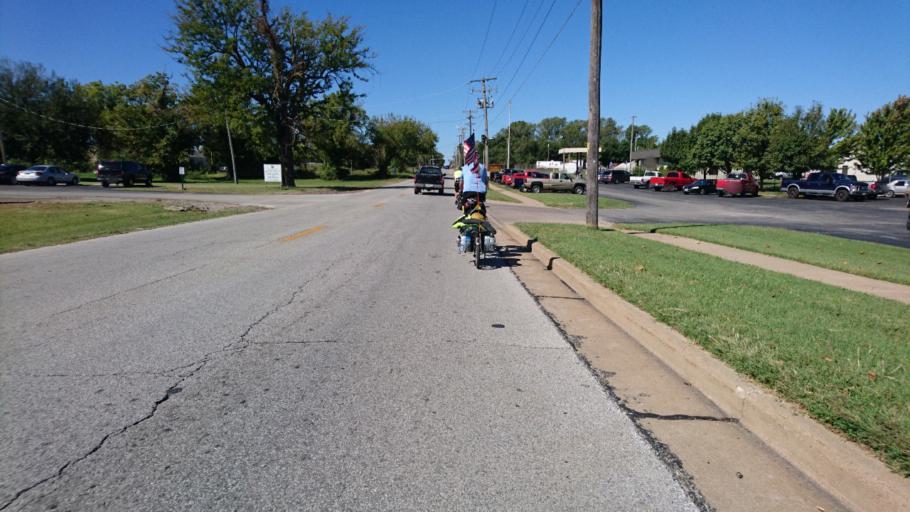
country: US
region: Missouri
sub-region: Jasper County
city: Joplin
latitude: 37.0901
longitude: -94.5264
